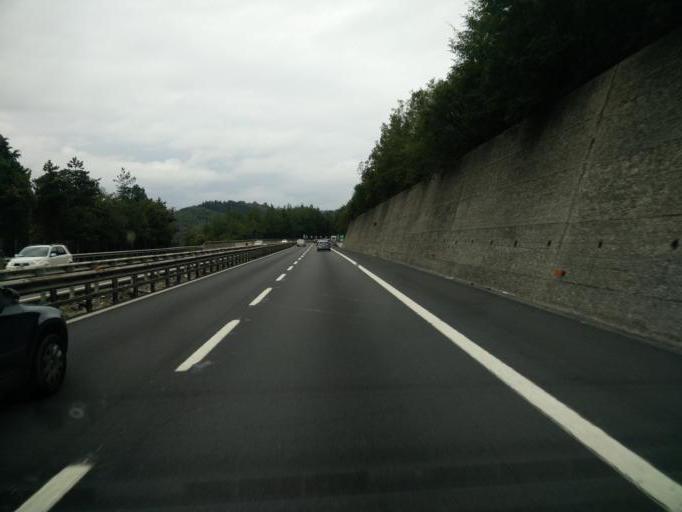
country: IT
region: Tuscany
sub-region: Province of Florence
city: Carraia
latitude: 43.9302
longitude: 11.2189
